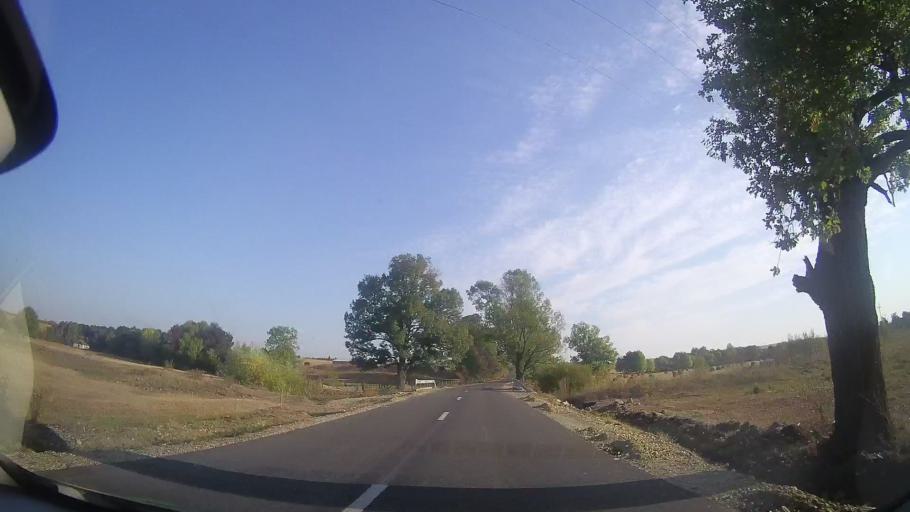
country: RO
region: Timis
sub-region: Comuna Masloc
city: Masloc
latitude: 45.9738
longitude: 21.4957
